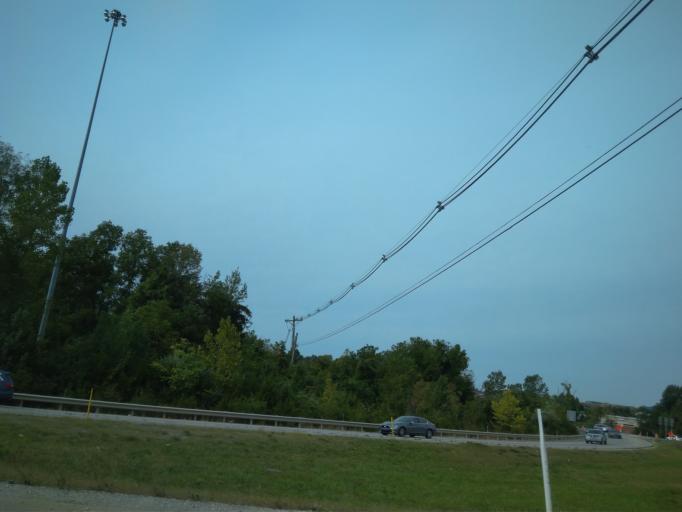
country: US
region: Kentucky
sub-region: Jefferson County
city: Anchorage
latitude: 38.2686
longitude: -85.5026
